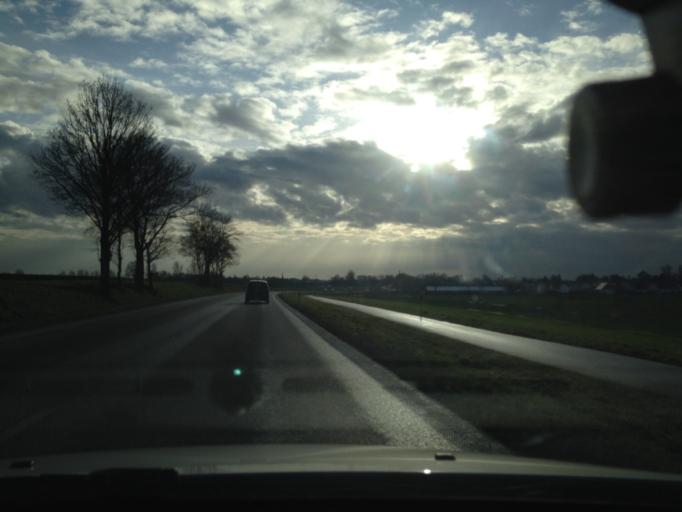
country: DE
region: Bavaria
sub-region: Swabia
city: Grossaitingen
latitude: 48.2138
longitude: 10.7750
